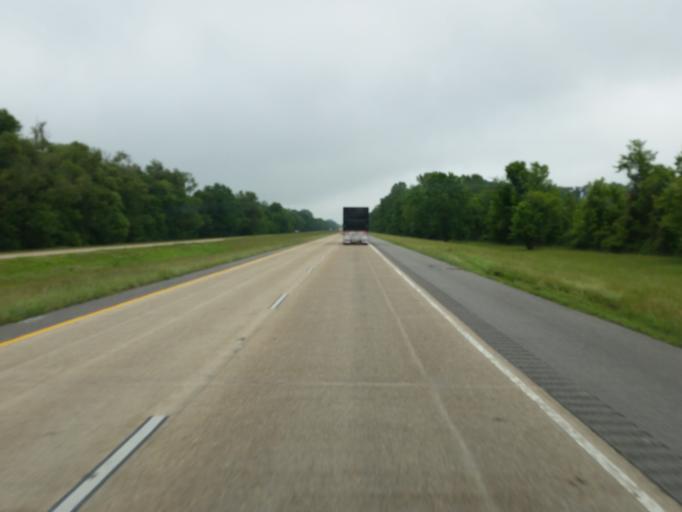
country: US
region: Louisiana
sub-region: Madison Parish
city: Tallulah
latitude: 32.3562
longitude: -91.1023
